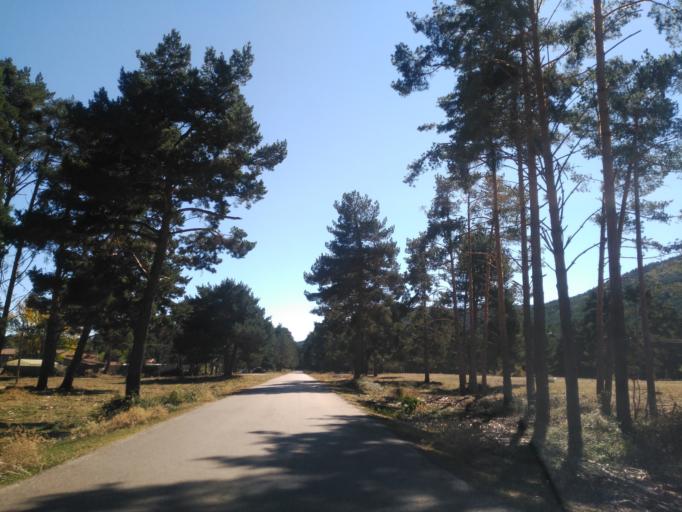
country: ES
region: Castille and Leon
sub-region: Provincia de Soria
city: Vinuesa
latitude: 41.9376
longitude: -2.7787
